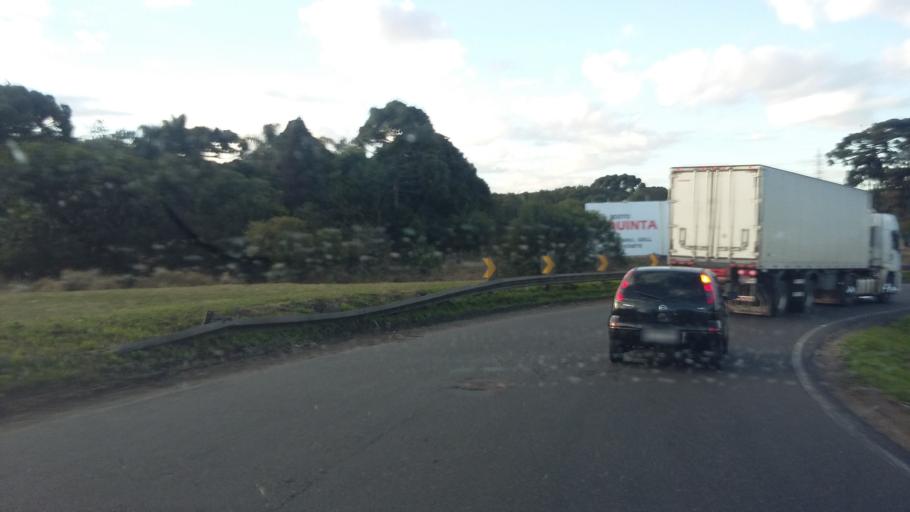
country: BR
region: Parana
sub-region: Curitiba
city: Curitiba
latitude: -25.4296
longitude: -49.3661
